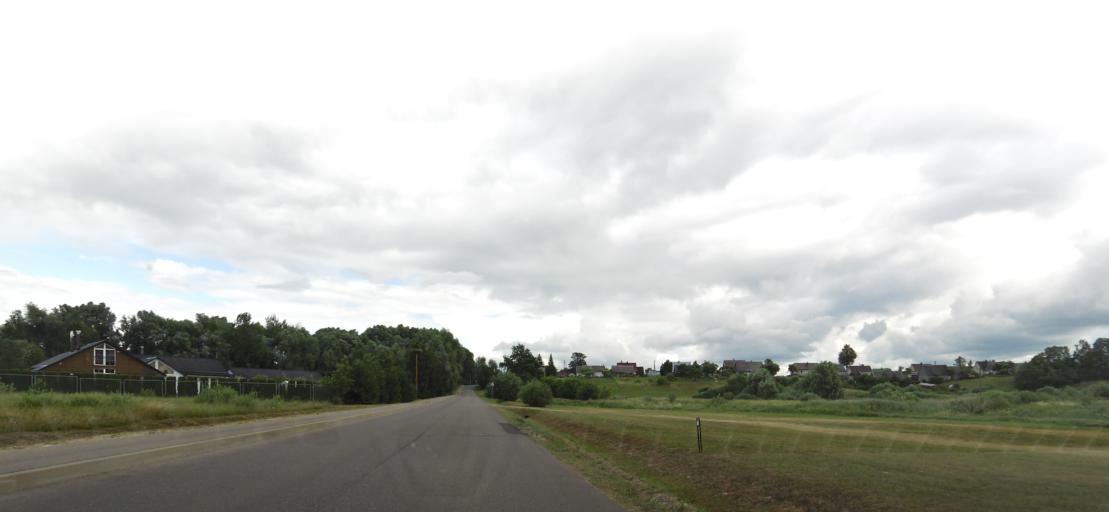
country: LT
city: Kupiskis
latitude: 55.8493
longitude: 24.9792
